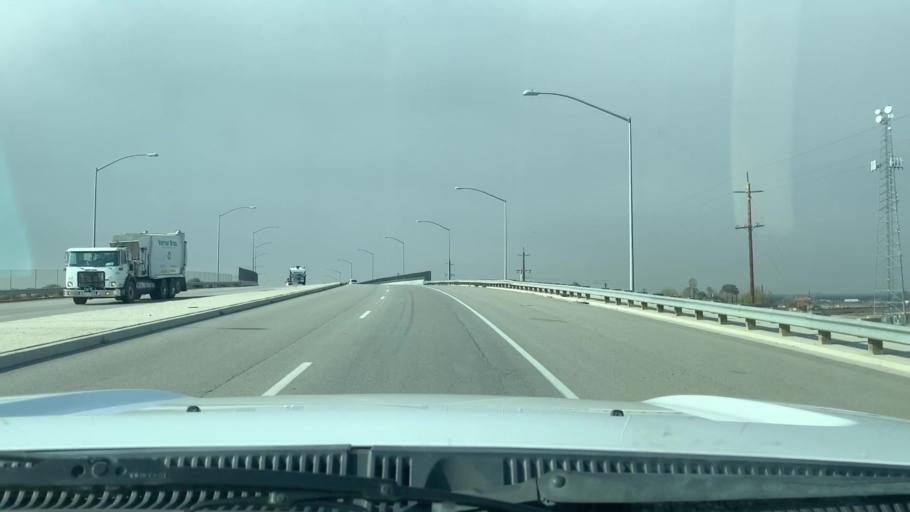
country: US
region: California
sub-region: Kern County
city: Rosedale
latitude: 35.4419
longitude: -119.1968
